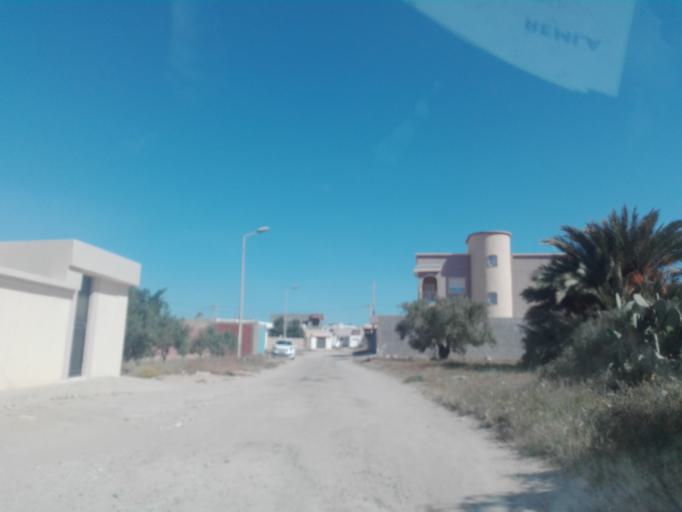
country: TN
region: Safaqis
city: Al Qarmadah
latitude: 34.7089
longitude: 11.1993
